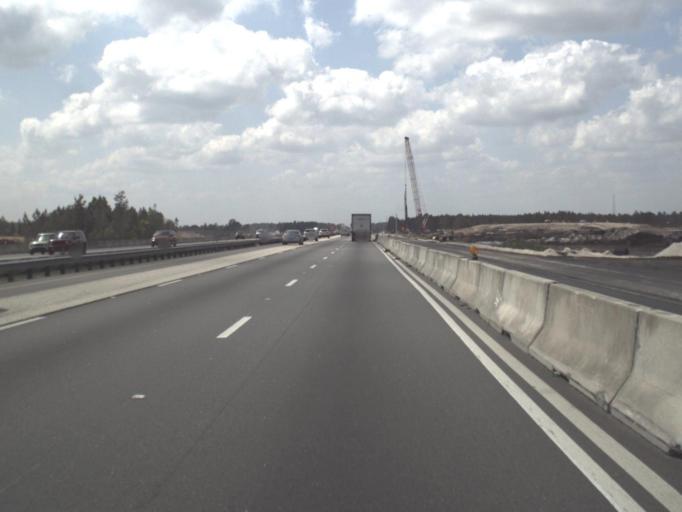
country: US
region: Florida
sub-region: Saint Johns County
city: Fruit Cove
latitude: 30.1105
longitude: -81.5099
